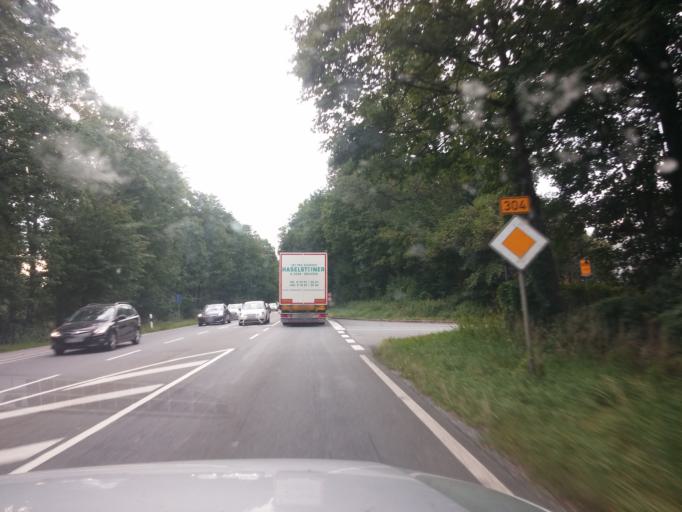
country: DE
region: Bavaria
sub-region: Upper Bavaria
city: Vaterstetten
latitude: 48.0949
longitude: 11.7750
